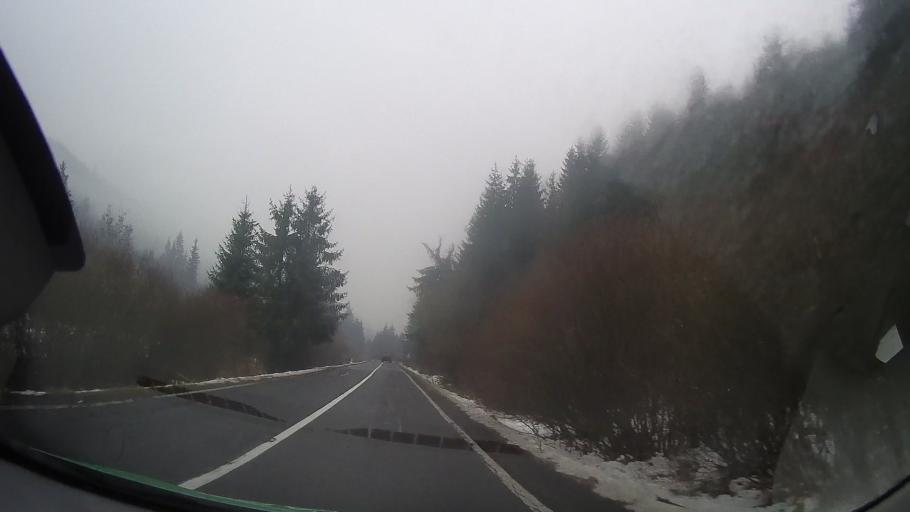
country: RO
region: Harghita
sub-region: Municipiul Gheorgheni
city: Gheorgheni
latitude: 46.7533
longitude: 25.6910
